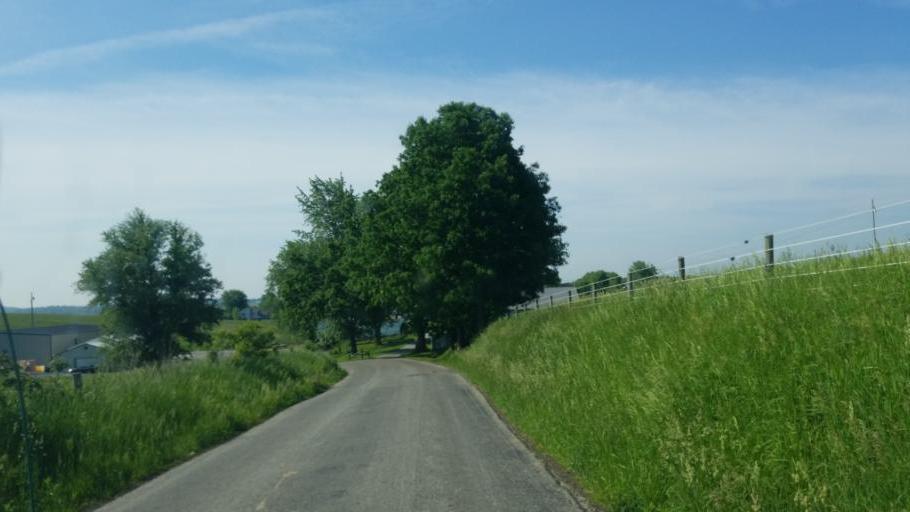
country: US
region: Ohio
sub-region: Tuscarawas County
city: Sugarcreek
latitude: 40.4912
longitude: -81.7700
